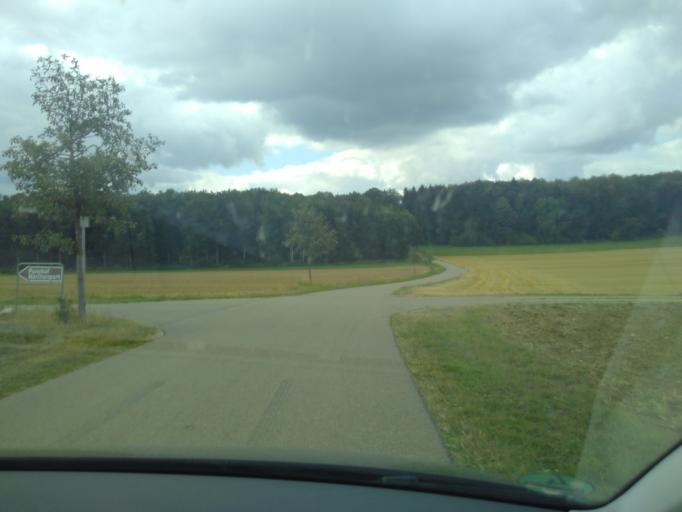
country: DE
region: Baden-Wuerttemberg
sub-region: Tuebingen Region
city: Berghulen
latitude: 48.4832
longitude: 9.7341
